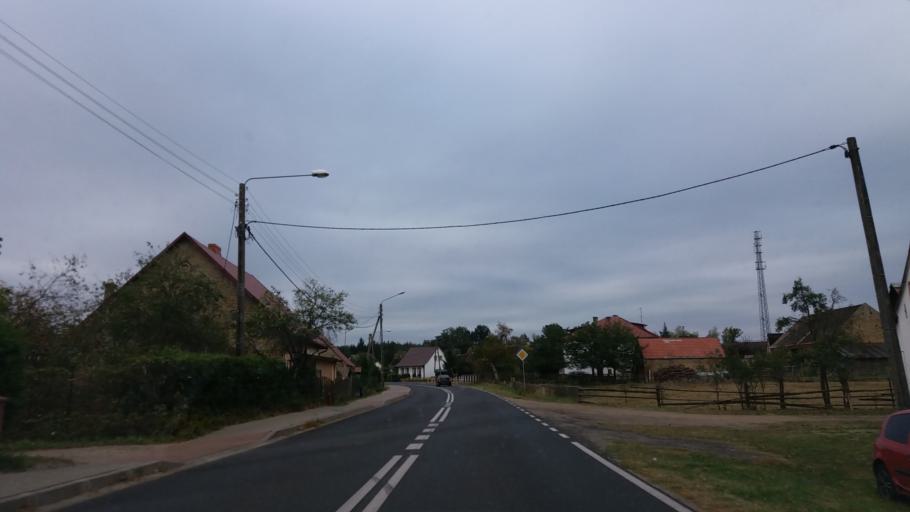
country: PL
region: Lubusz
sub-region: Powiat gorzowski
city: Klodawa
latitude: 52.8852
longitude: 15.1909
